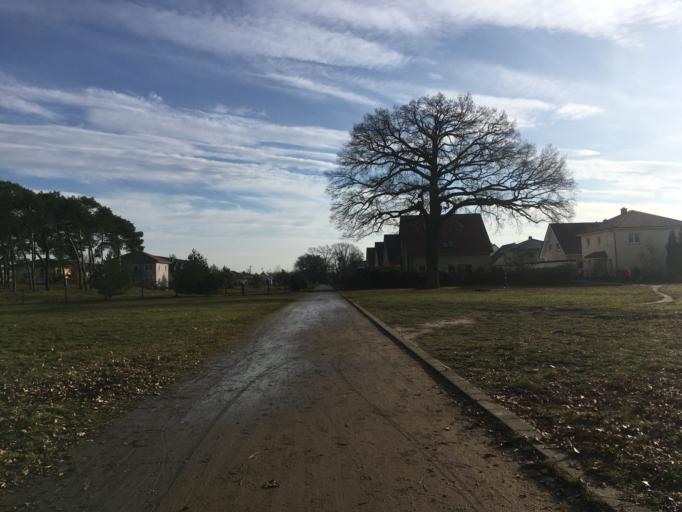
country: DE
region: Berlin
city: Karlshorst
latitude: 52.4779
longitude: 13.5280
